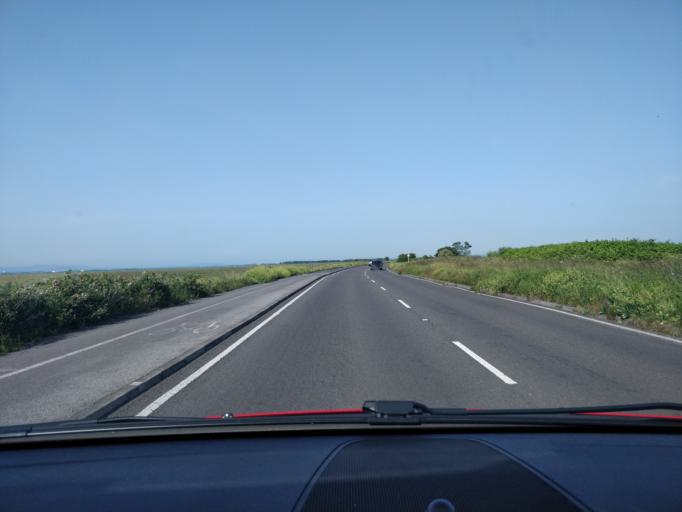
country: GB
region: England
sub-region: Sefton
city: Southport
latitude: 53.6826
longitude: -2.9689
